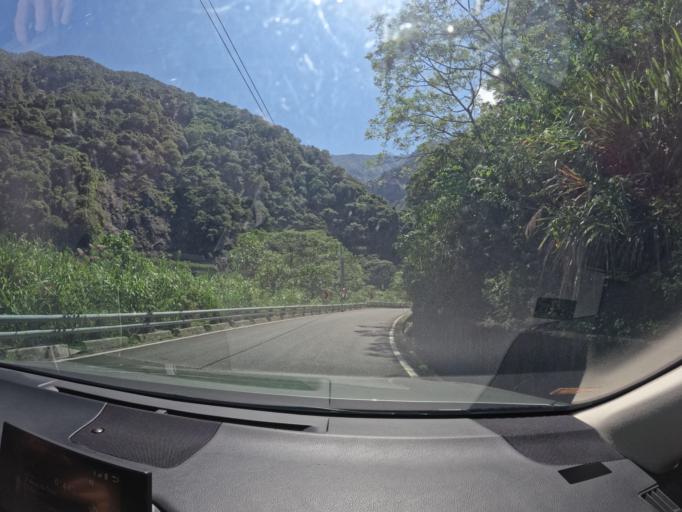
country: TW
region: Taiwan
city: Yujing
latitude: 23.2590
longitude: 120.8491
